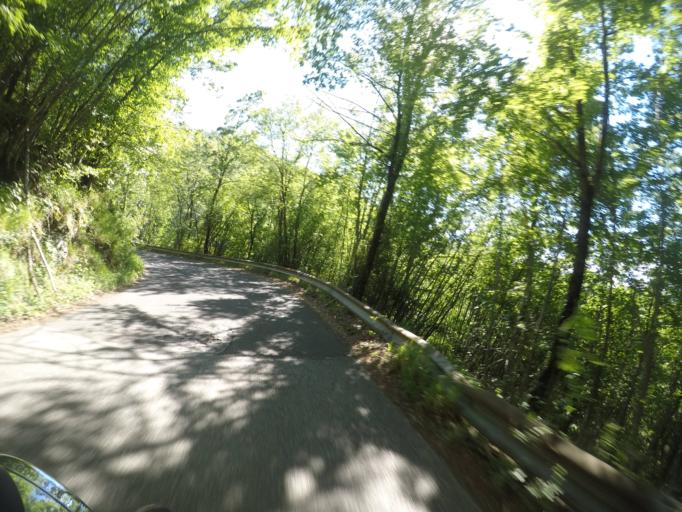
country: IT
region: Tuscany
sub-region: Provincia di Massa-Carrara
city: Fosdinovo
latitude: 44.1318
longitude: 10.0681
